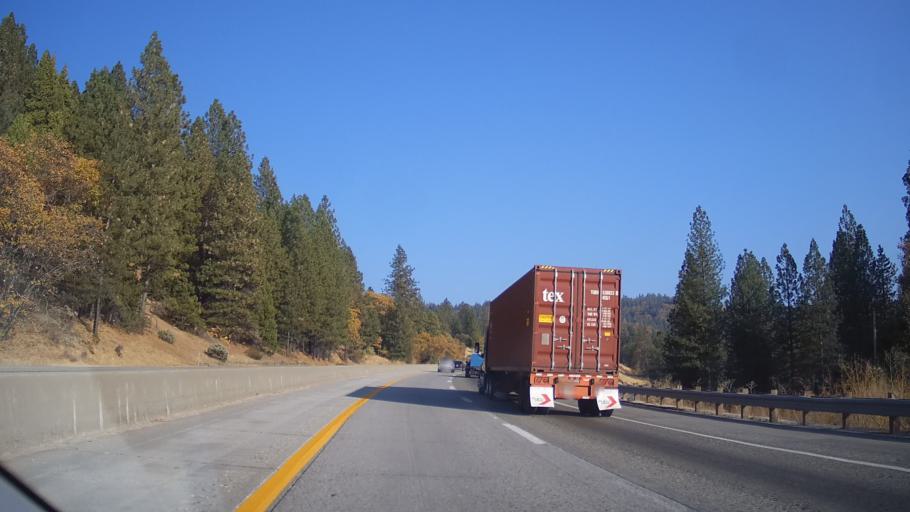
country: US
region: California
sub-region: Placer County
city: Colfax
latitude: 39.2031
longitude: -120.8057
